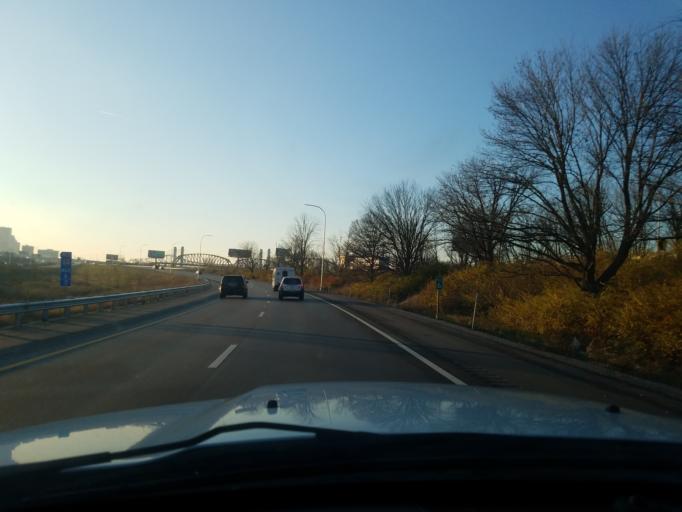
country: US
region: Indiana
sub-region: Clark County
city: Jeffersonville
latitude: 38.2620
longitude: -85.7277
